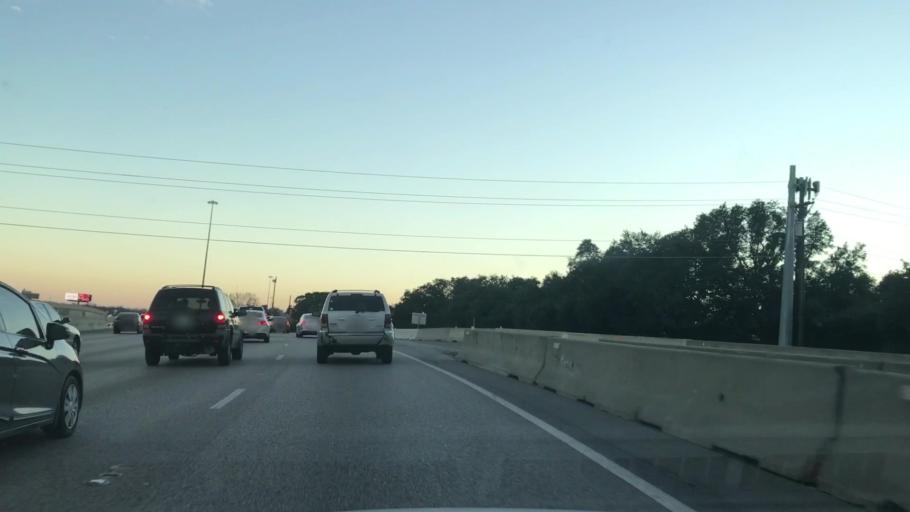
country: US
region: Texas
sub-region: Dallas County
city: Dallas
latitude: 32.7386
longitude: -96.8239
